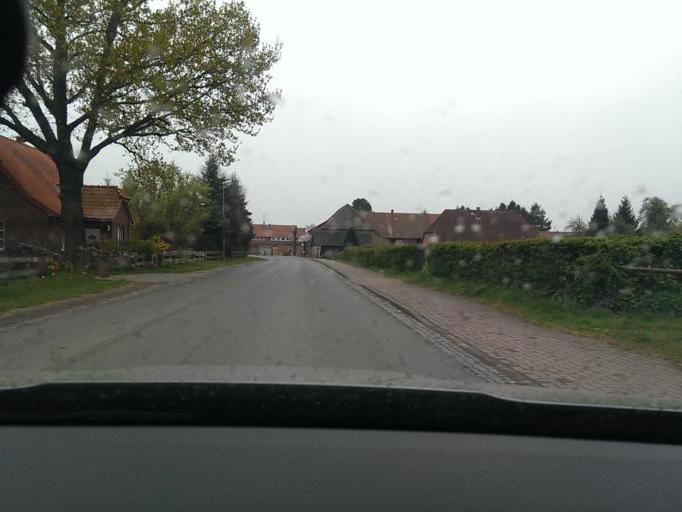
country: DE
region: Lower Saxony
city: Steimbke
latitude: 52.6472
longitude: 9.4914
